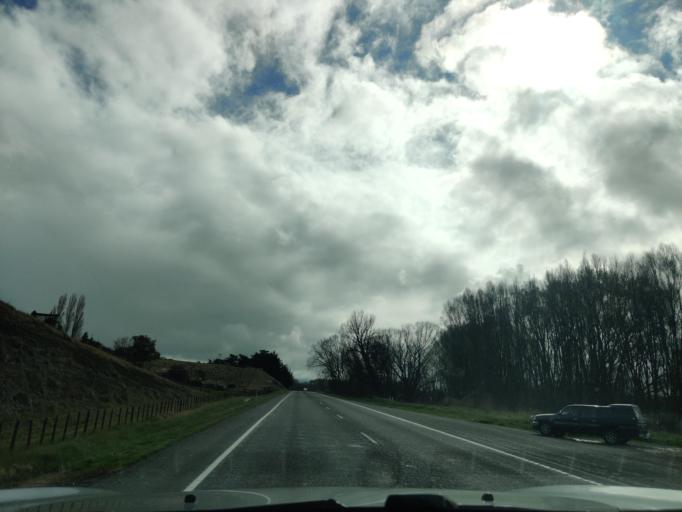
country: NZ
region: Hawke's Bay
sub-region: Hastings District
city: Hastings
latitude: -39.9772
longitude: 176.5003
